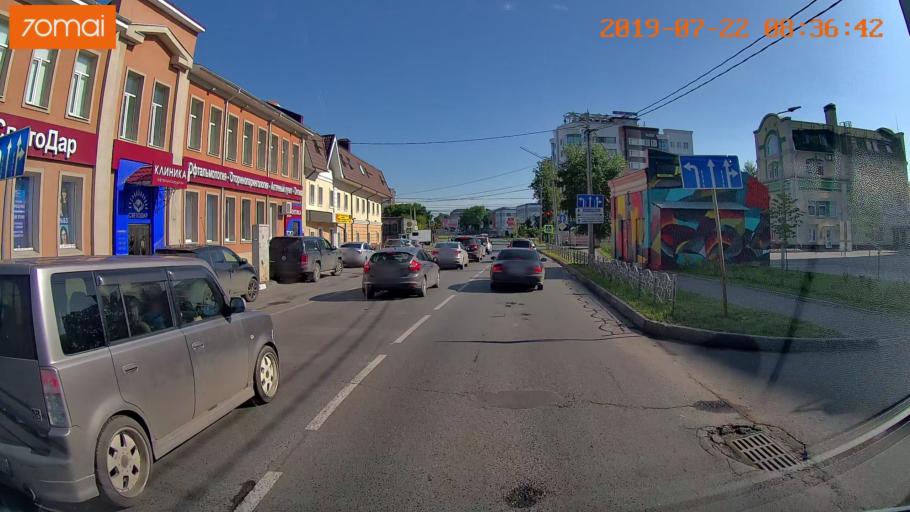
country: RU
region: Ivanovo
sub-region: Gorod Ivanovo
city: Ivanovo
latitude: 56.9907
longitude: 40.9892
